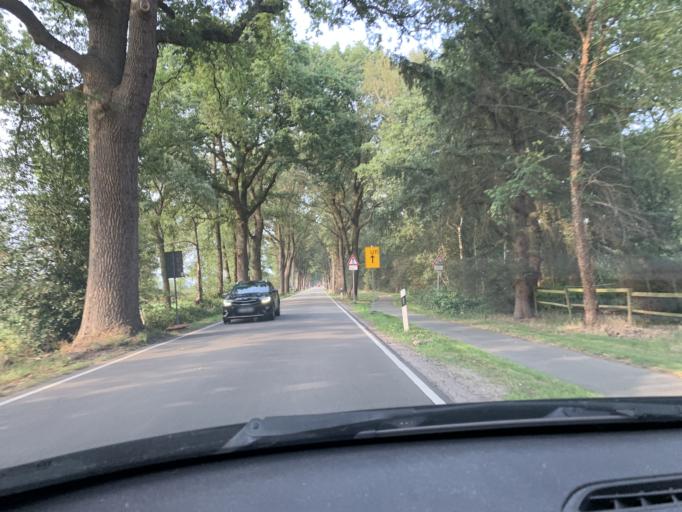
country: DE
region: Lower Saxony
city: Apen
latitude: 53.1820
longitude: 7.7813
